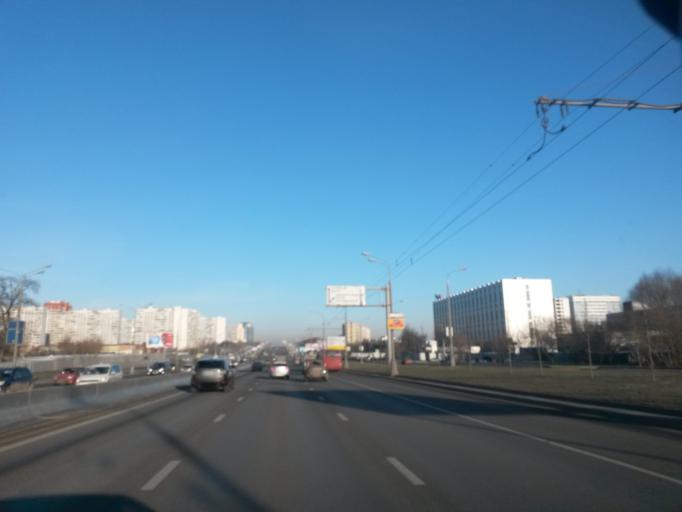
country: RU
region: Moscow
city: Chertanovo Yuzhnoye
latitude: 55.6173
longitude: 37.6126
